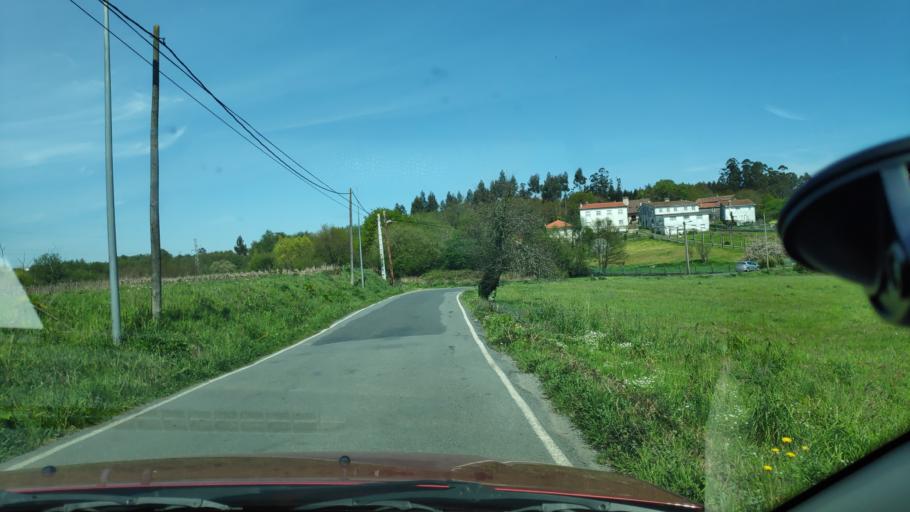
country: ES
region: Galicia
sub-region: Provincia da Coruna
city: Santiago de Compostela
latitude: 42.8939
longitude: -8.5249
